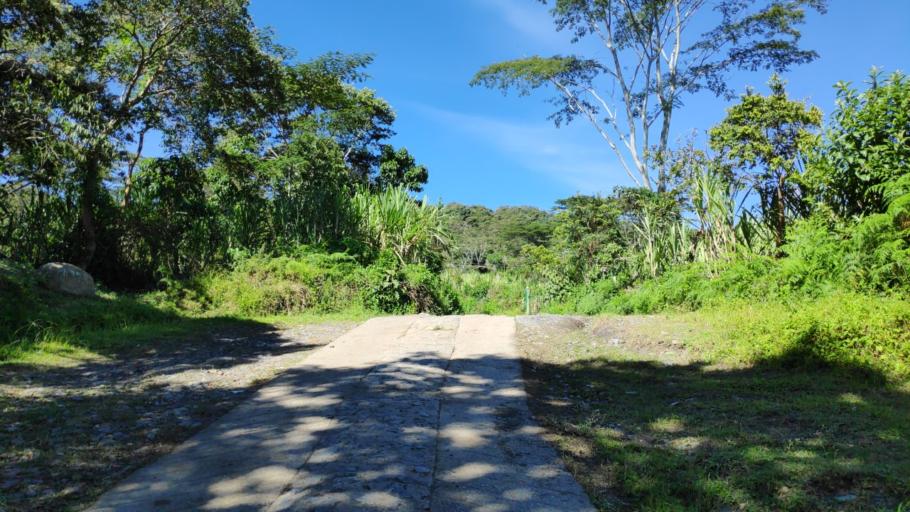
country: CO
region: Santander
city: Guepsa
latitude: 5.9875
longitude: -73.5435
